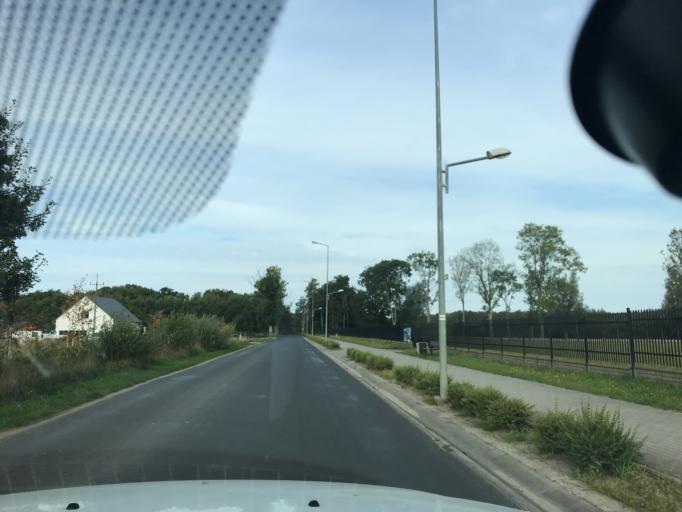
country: PL
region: West Pomeranian Voivodeship
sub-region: Powiat slawienski
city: Slawno
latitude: 54.5343
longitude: 16.5758
